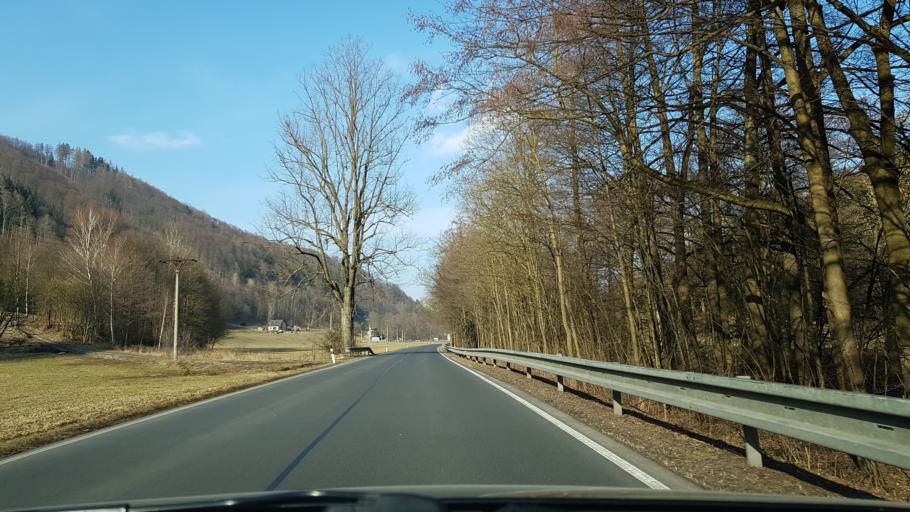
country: CZ
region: Olomoucky
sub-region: Okres Sumperk
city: Hanusovice
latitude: 50.0491
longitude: 16.9156
